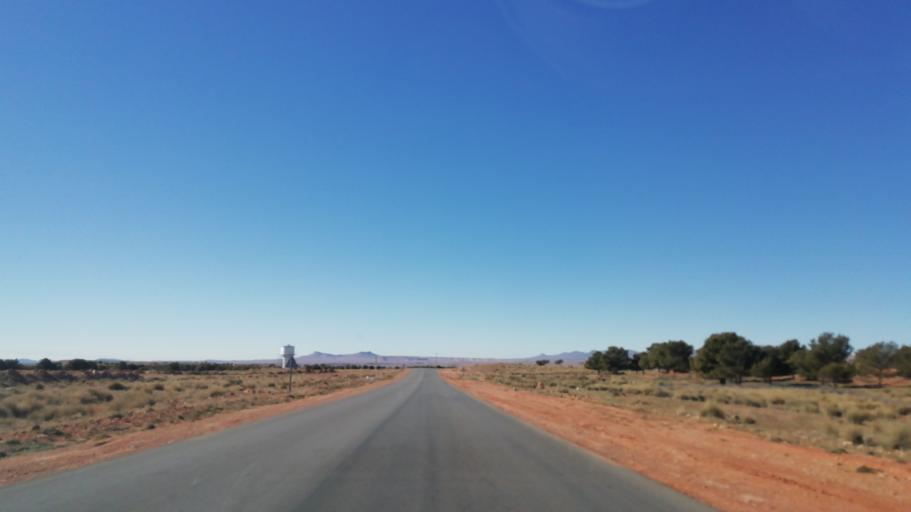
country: DZ
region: El Bayadh
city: El Bayadh
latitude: 33.6325
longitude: 1.3677
